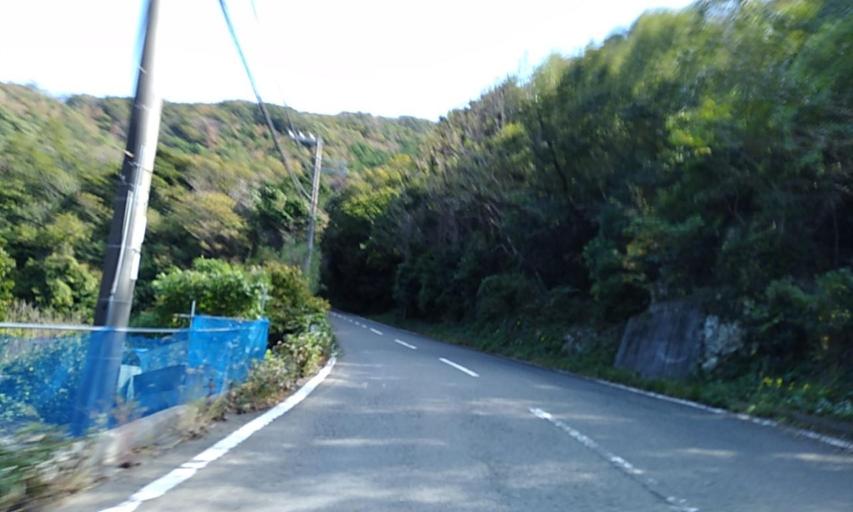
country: JP
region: Wakayama
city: Gobo
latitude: 33.9665
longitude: 135.0919
